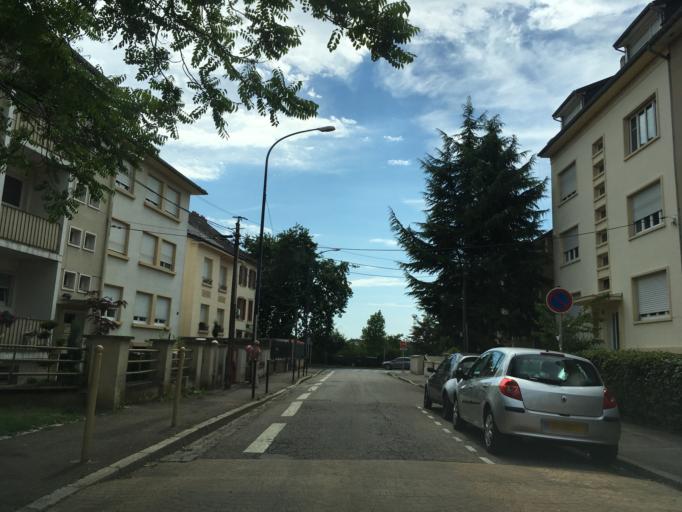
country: FR
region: Lorraine
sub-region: Departement de la Moselle
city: Montigny-les-Metz
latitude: 49.0978
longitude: 6.1706
